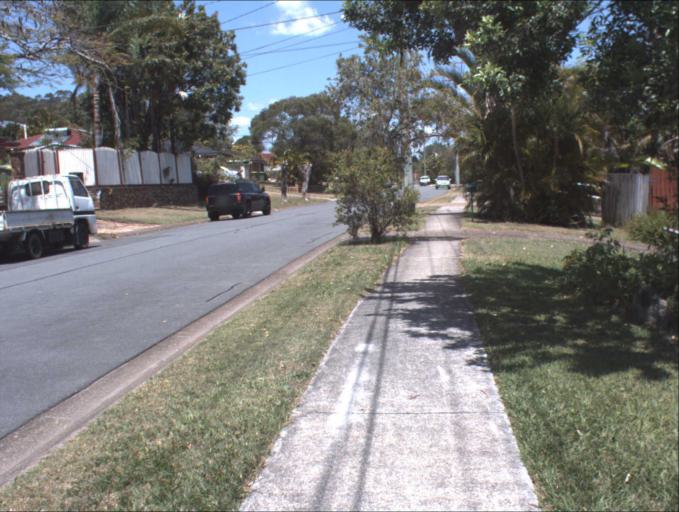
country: AU
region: Queensland
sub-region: Logan
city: Springwood
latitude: -27.6017
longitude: 153.1414
